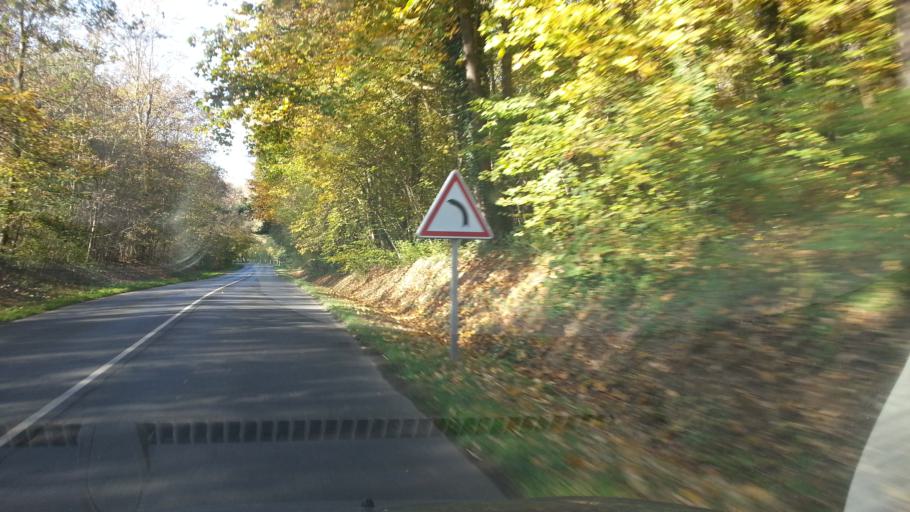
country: FR
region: Picardie
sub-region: Departement de l'Oise
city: Cires-les-Mello
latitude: 49.2667
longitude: 2.3786
